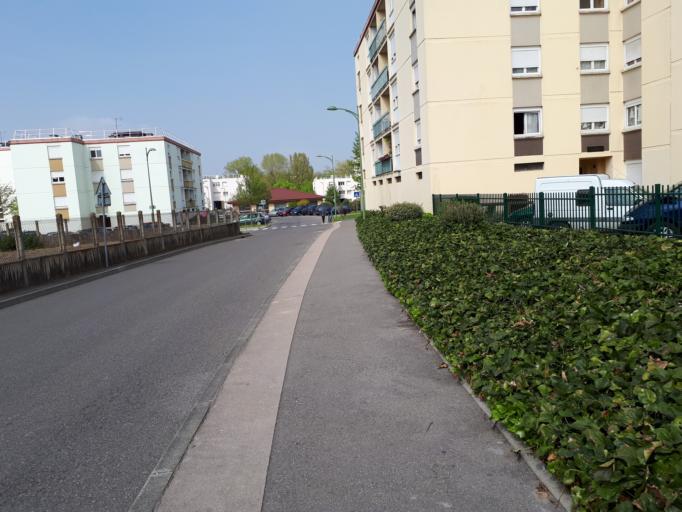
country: FR
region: Rhone-Alpes
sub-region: Departement de l'Isere
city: Bourgoin-Jallieu
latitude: 45.6071
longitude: 5.2690
